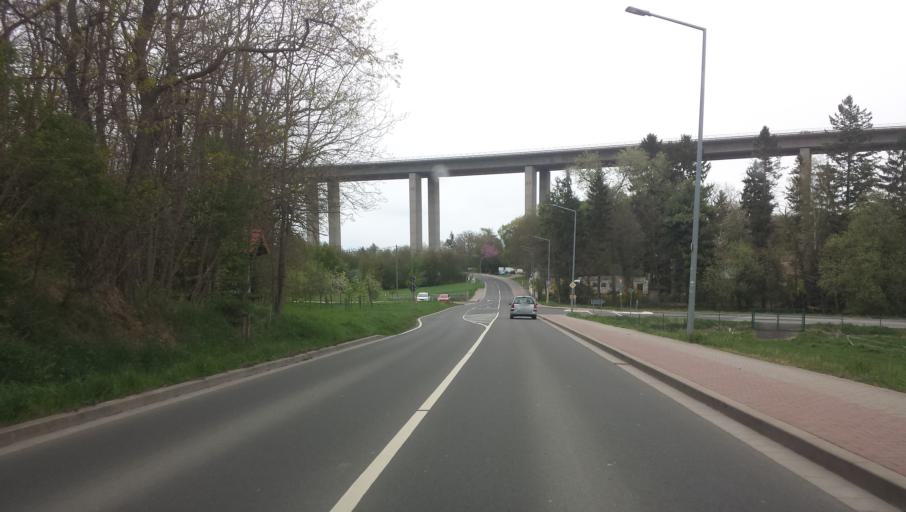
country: DE
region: Rheinland-Pfalz
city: Freimersheim
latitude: 49.7364
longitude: 8.0794
